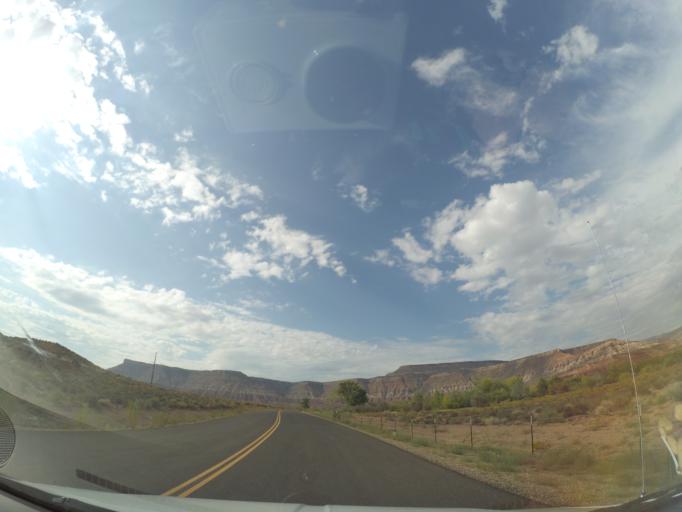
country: US
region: Utah
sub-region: Washington County
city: LaVerkin
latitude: 37.2088
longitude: -113.1747
